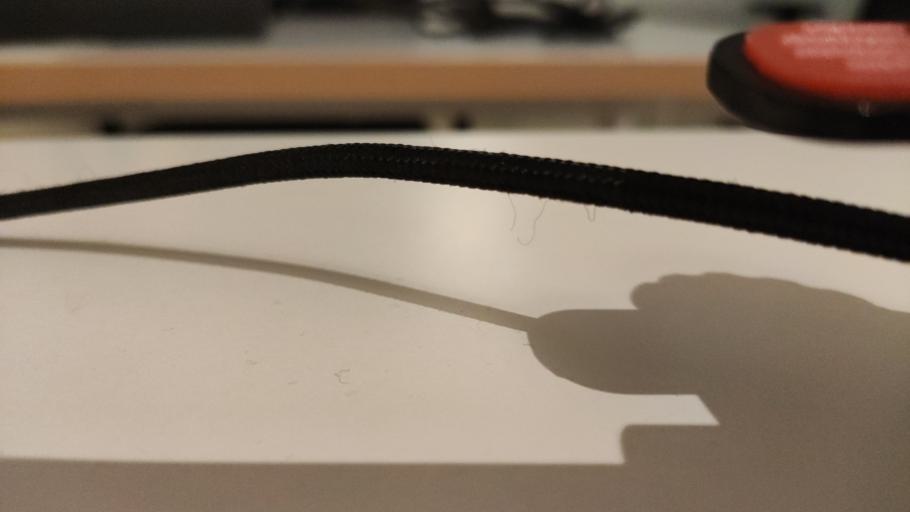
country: RU
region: Moskovskaya
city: Novoye
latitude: 55.6301
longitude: 38.9424
